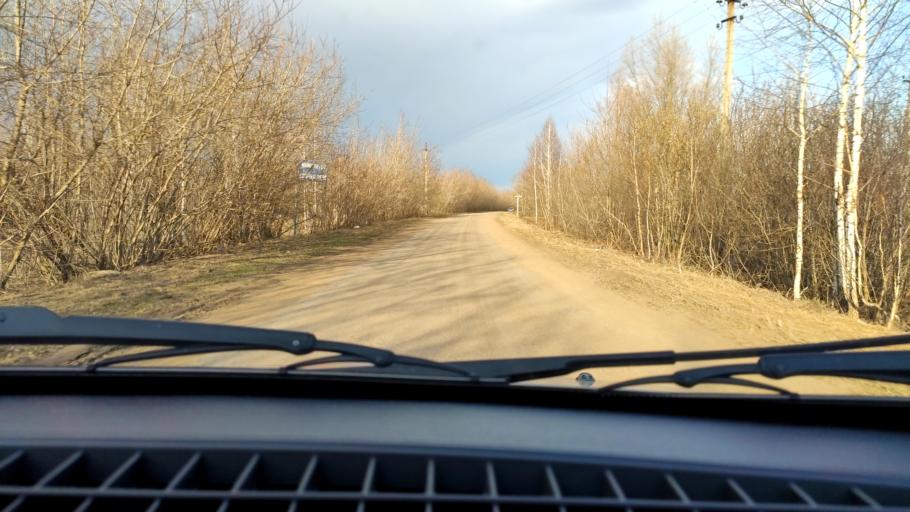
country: RU
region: Bashkortostan
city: Iglino
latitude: 54.8463
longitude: 56.4706
